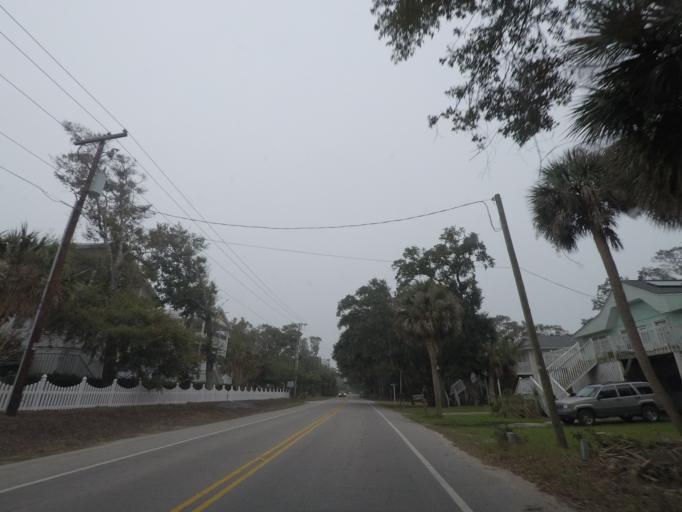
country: US
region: South Carolina
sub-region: Charleston County
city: Seabrook Island
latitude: 32.4930
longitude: -80.3169
